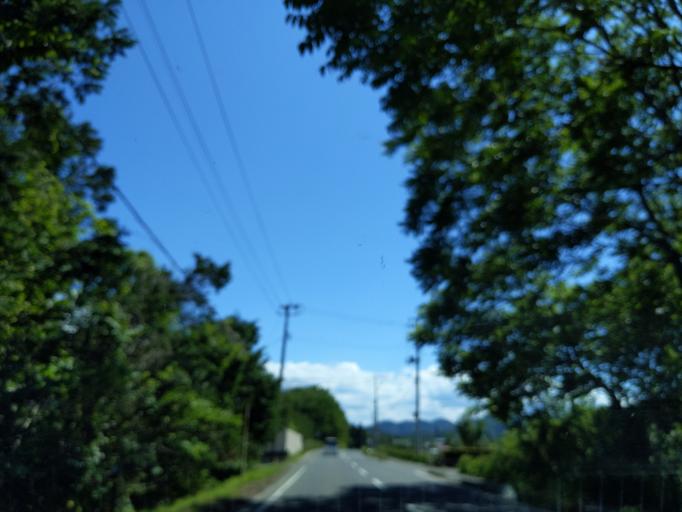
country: JP
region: Fukushima
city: Koriyama
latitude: 37.3950
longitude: 140.2678
